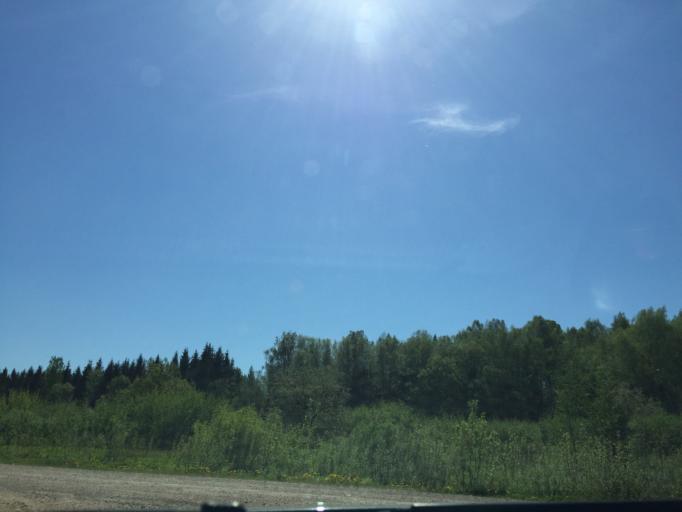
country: LV
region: Malpils
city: Malpils
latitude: 56.9637
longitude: 24.8280
